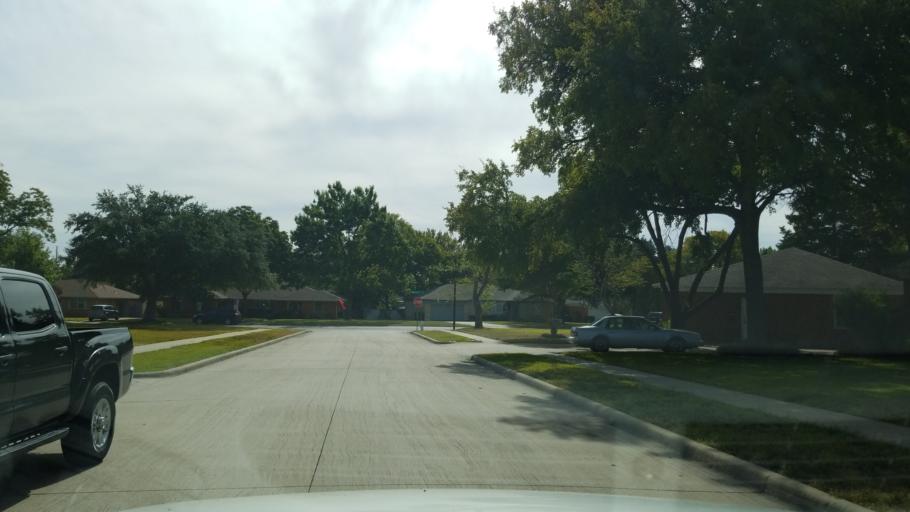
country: US
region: Texas
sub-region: Dallas County
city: Garland
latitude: 32.8967
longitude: -96.6547
